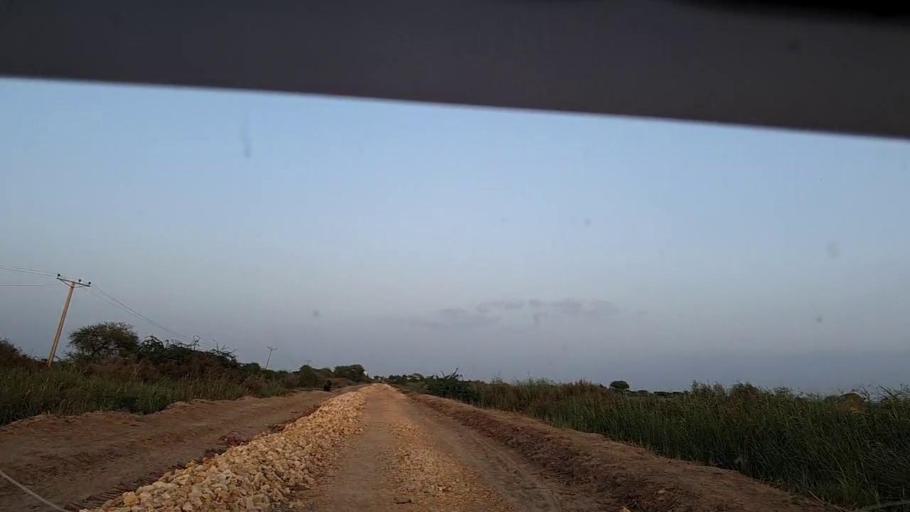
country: PK
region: Sindh
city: Kadhan
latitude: 24.5293
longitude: 68.9510
